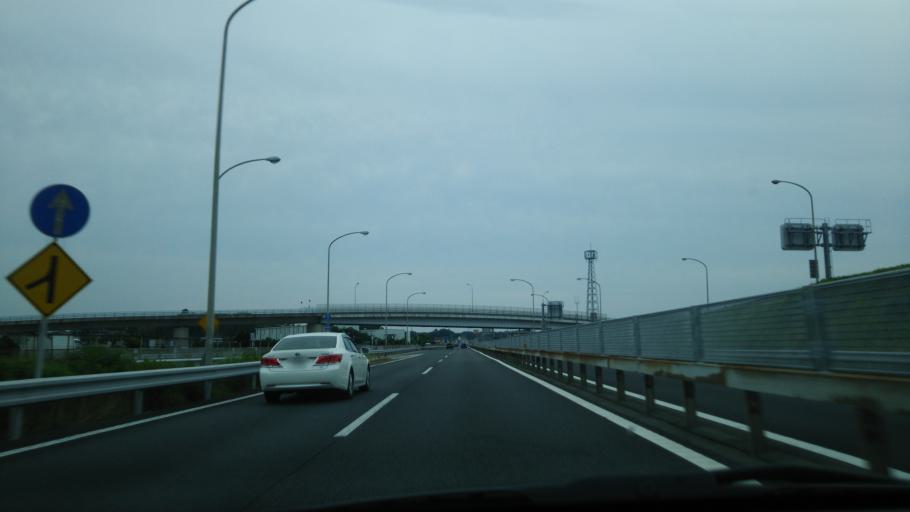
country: JP
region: Kanagawa
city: Isehara
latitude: 35.3637
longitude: 139.3067
